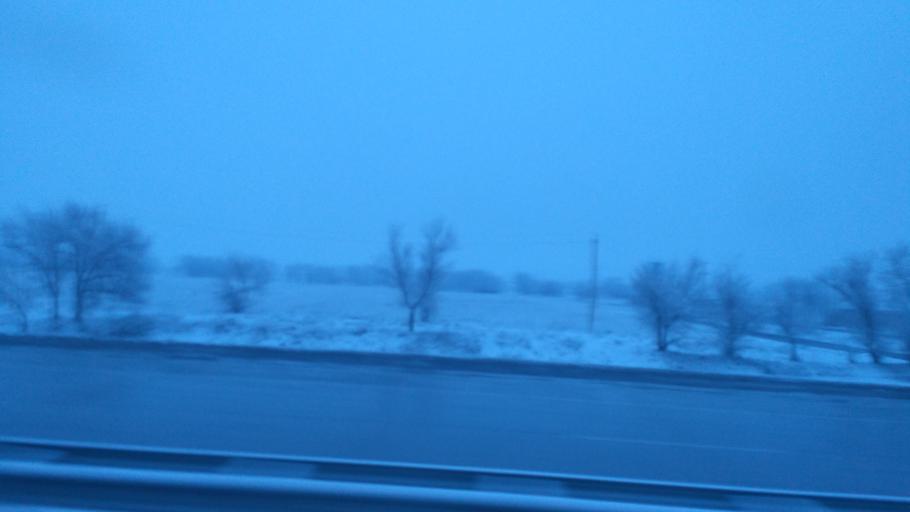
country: KZ
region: Ongtustik Qazaqstan
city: Shymkent
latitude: 42.4330
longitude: 69.4299
